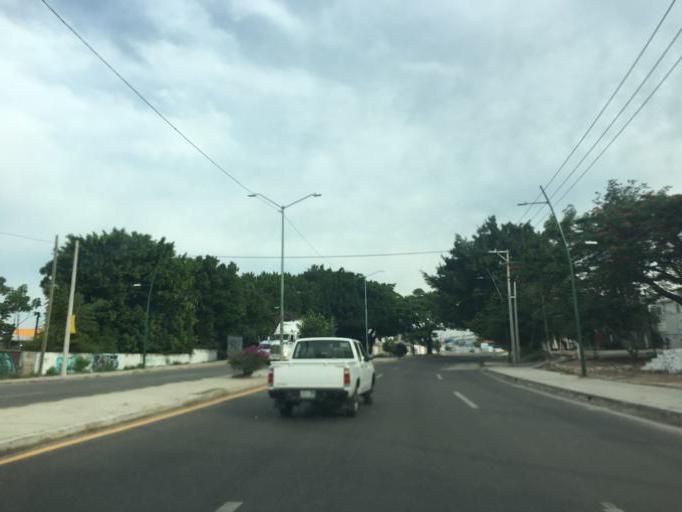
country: MX
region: Chiapas
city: Tuxtla Gutierrez
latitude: 16.7645
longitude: -93.1616
